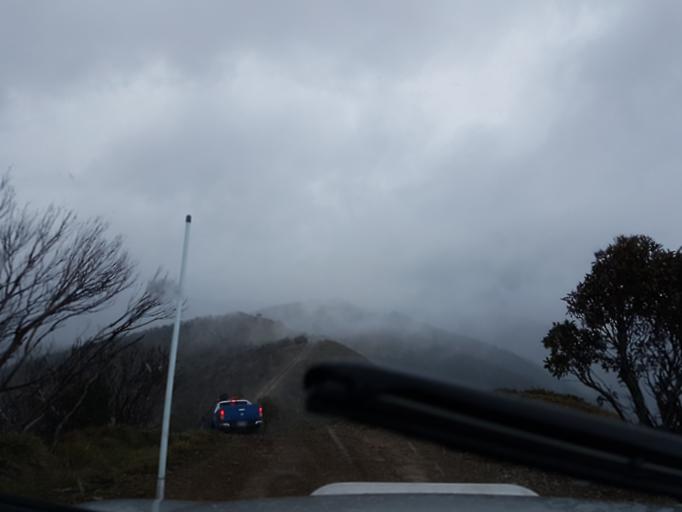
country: AU
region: Victoria
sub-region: Alpine
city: Mount Beauty
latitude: -37.0964
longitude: 147.0548
